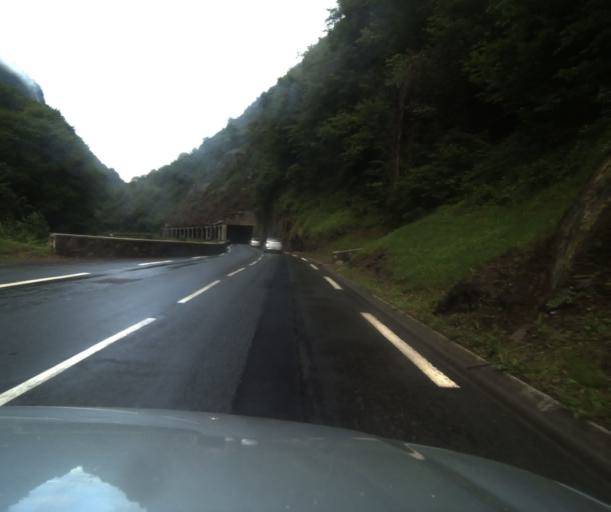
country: FR
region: Midi-Pyrenees
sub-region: Departement des Hautes-Pyrenees
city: Pierrefitte-Nestalas
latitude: 42.9276
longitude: -0.0419
